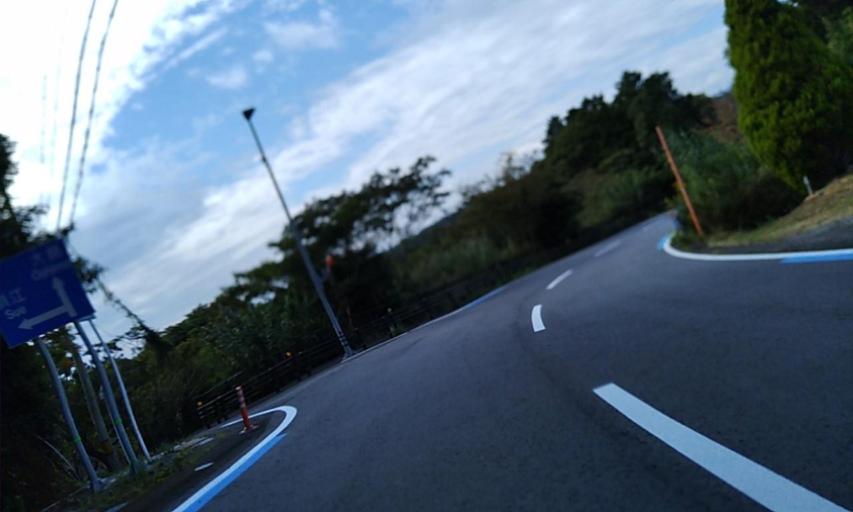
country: JP
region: Wakayama
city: Shingu
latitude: 33.4661
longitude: 135.8288
